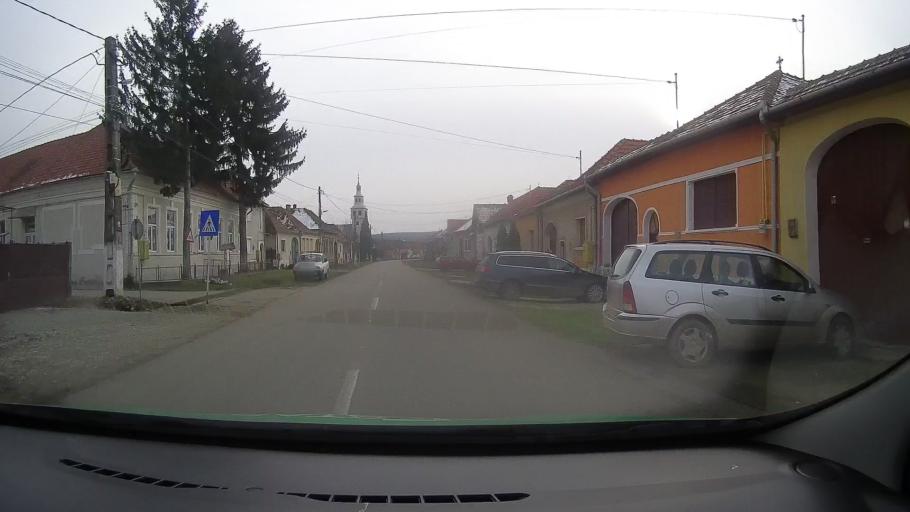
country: RO
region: Hunedoara
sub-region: Comuna Turdas
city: Turdas
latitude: 45.8512
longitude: 23.1230
